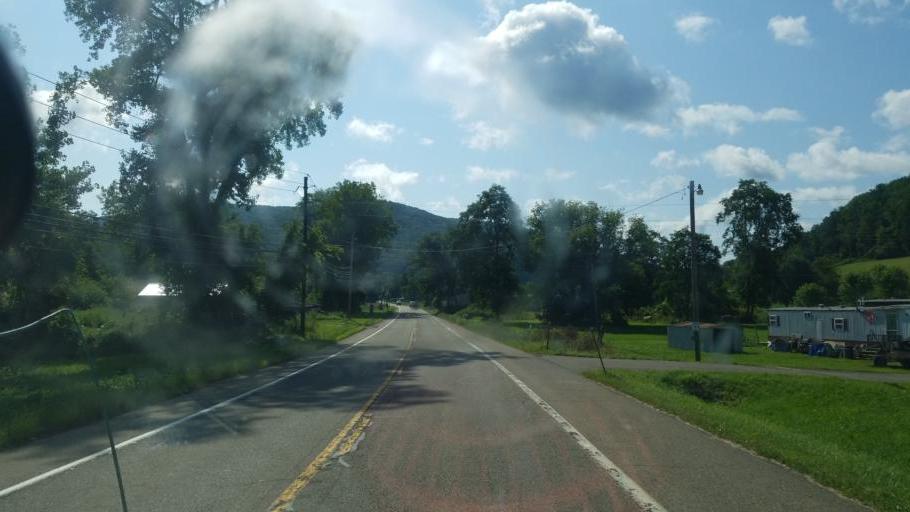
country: US
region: New York
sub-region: Steuben County
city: Canisteo
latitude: 42.2641
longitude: -77.5927
